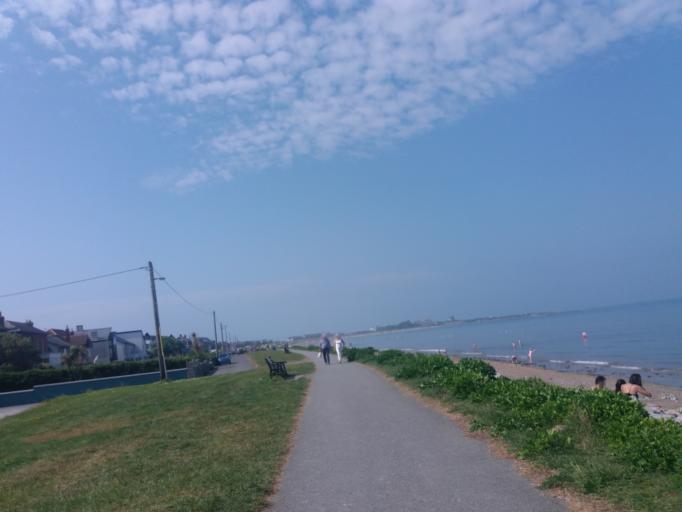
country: IE
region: Leinster
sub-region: Fingal County
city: Skerries
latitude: 53.5740
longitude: -6.1016
